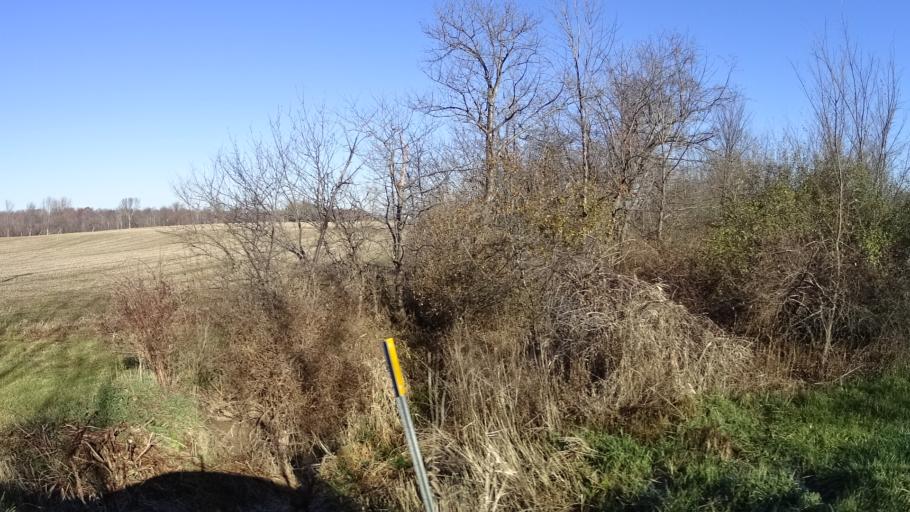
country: US
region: Ohio
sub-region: Lorain County
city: Wellington
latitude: 41.0700
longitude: -82.1829
